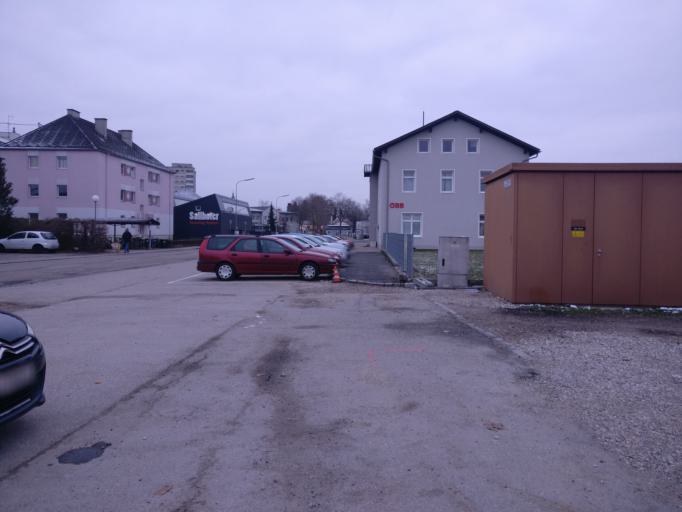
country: AT
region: Upper Austria
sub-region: Politischer Bezirk Braunau am Inn
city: Braunau am Inn
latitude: 48.2589
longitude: 13.0489
